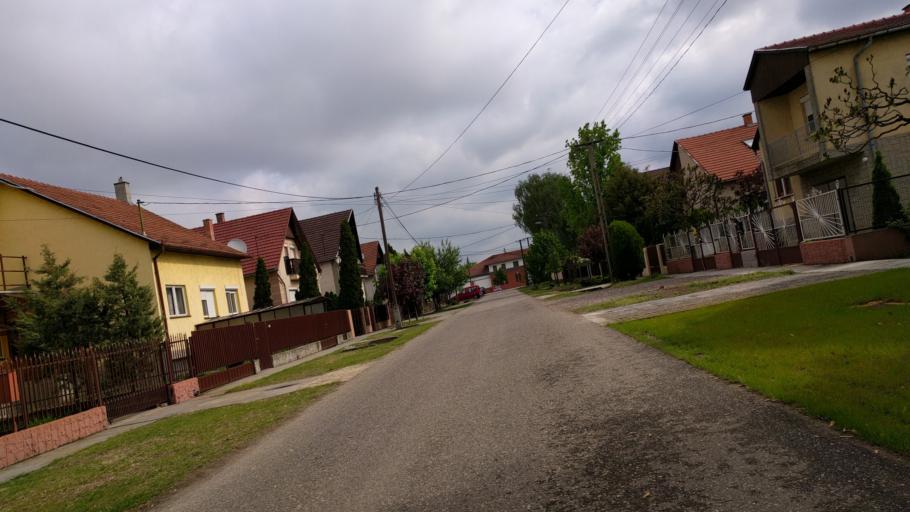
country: HU
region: Bacs-Kiskun
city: Tiszakecske
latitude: 46.9419
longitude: 20.0955
